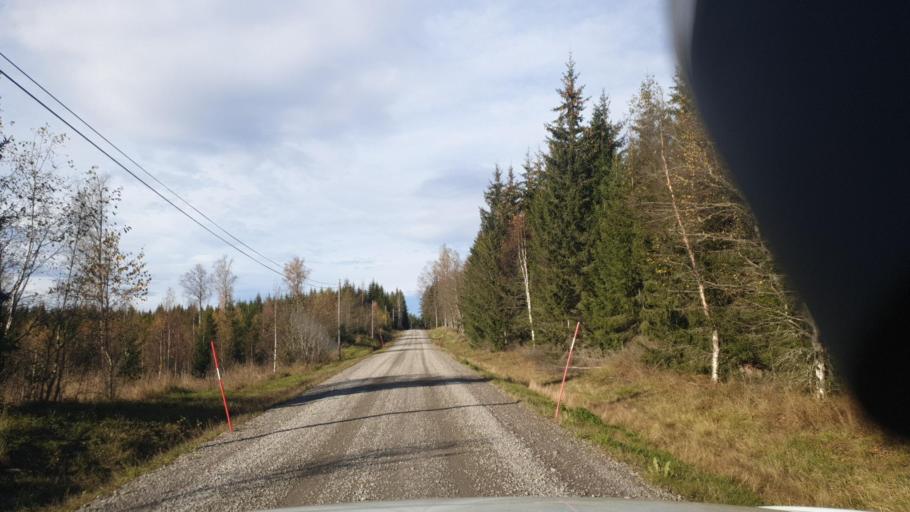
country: SE
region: Vaermland
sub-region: Eda Kommun
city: Charlottenberg
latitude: 59.9737
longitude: 12.4953
